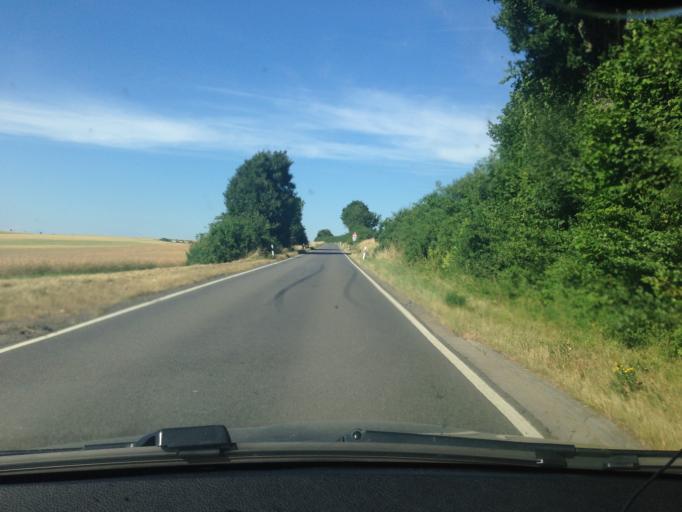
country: DE
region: Hesse
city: Ober-Ramstadt
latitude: 49.8335
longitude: 8.7584
